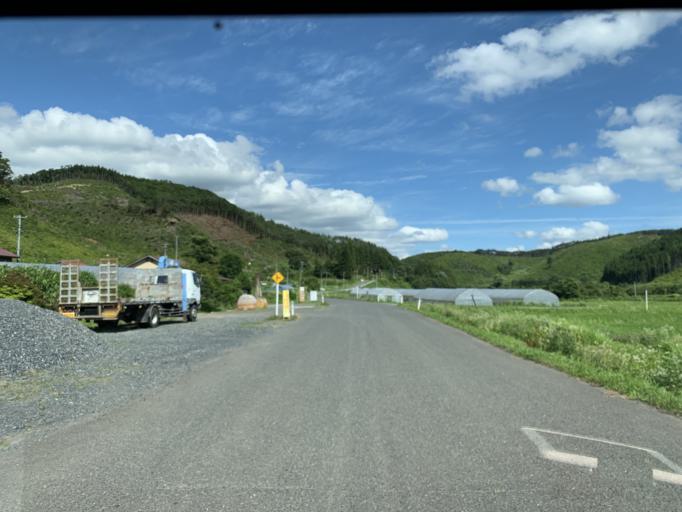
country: JP
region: Iwate
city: Ichinoseki
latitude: 38.9637
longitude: 140.9514
